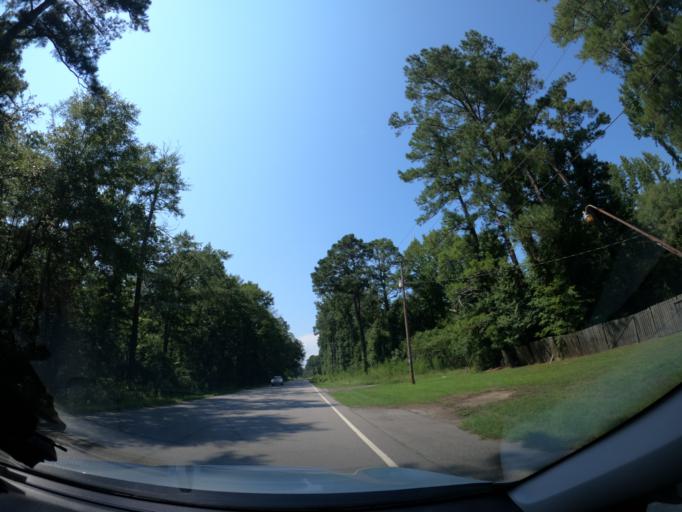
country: US
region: South Carolina
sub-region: Richland County
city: Hopkins
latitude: 33.8968
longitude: -80.9209
